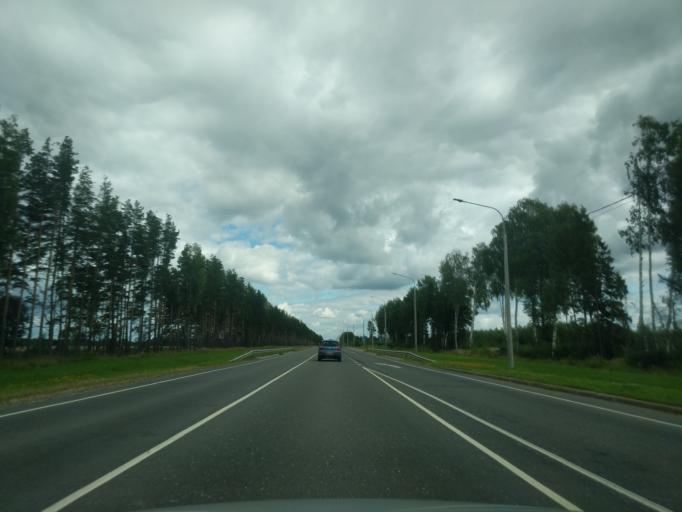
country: RU
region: Jaroslavl
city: Nekrasovskoye
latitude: 57.6105
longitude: 40.3365
